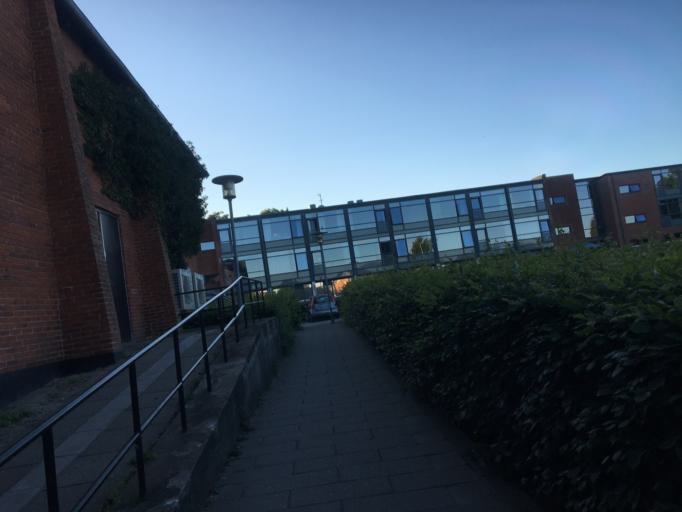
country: DK
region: Central Jutland
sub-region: Syddjurs Kommune
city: Hornslet
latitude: 56.3176
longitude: 10.3178
